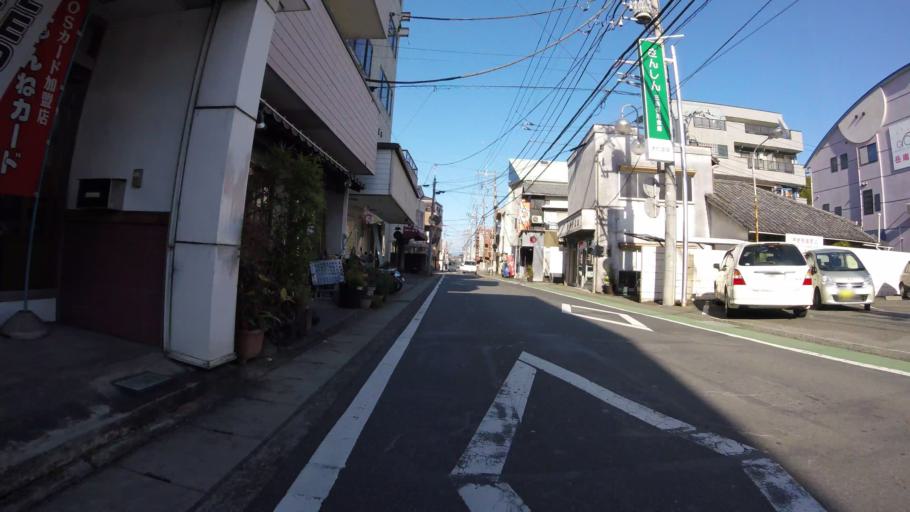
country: JP
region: Shizuoka
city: Mishima
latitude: 34.9947
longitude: 138.9388
